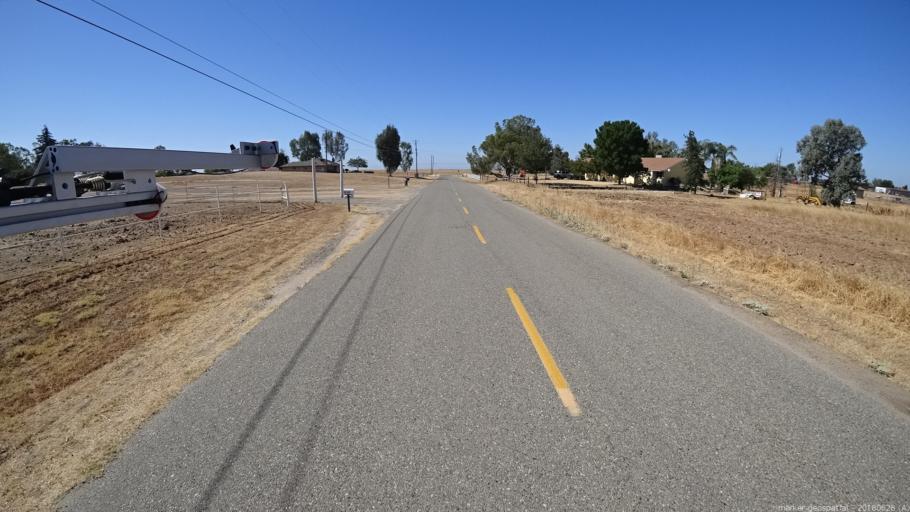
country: US
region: California
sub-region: Madera County
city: Bonadelle Ranchos-Madera Ranchos
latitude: 36.9979
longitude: -119.8612
